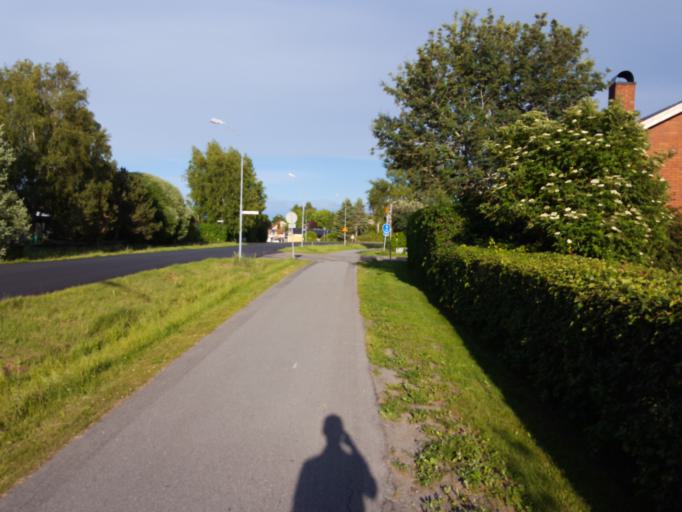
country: SE
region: Uppsala
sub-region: Osthammars Kommun
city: OEsthammar
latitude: 60.2606
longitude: 18.3532
